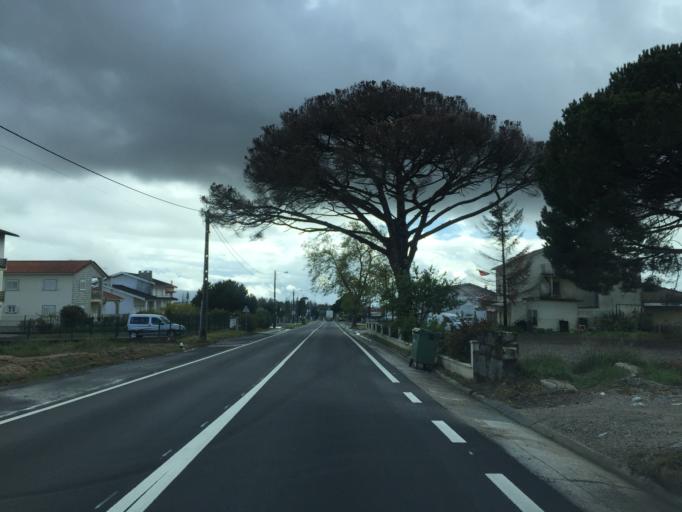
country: PT
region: Coimbra
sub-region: Oliveira do Hospital
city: Oliveira do Hospital
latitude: 40.3197
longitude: -7.8855
